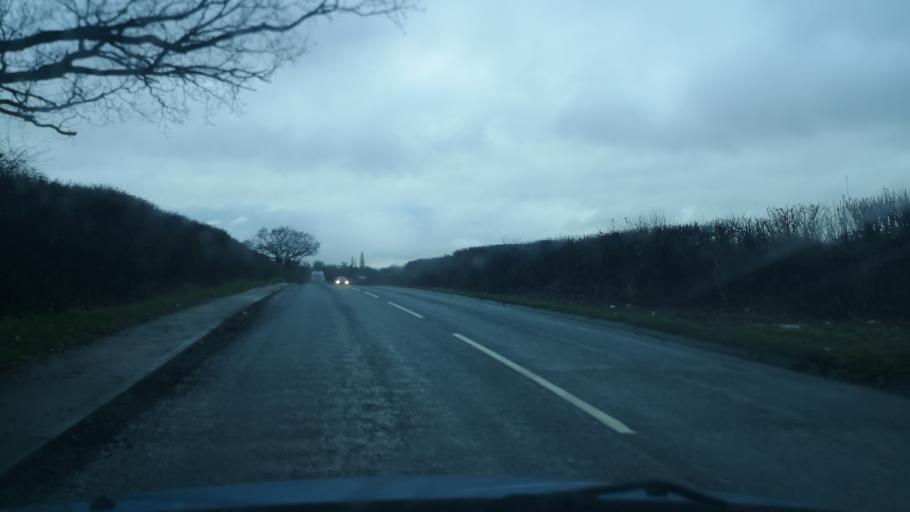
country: GB
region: England
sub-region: City and Borough of Wakefield
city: Fitzwilliam
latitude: 53.6426
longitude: -1.3857
